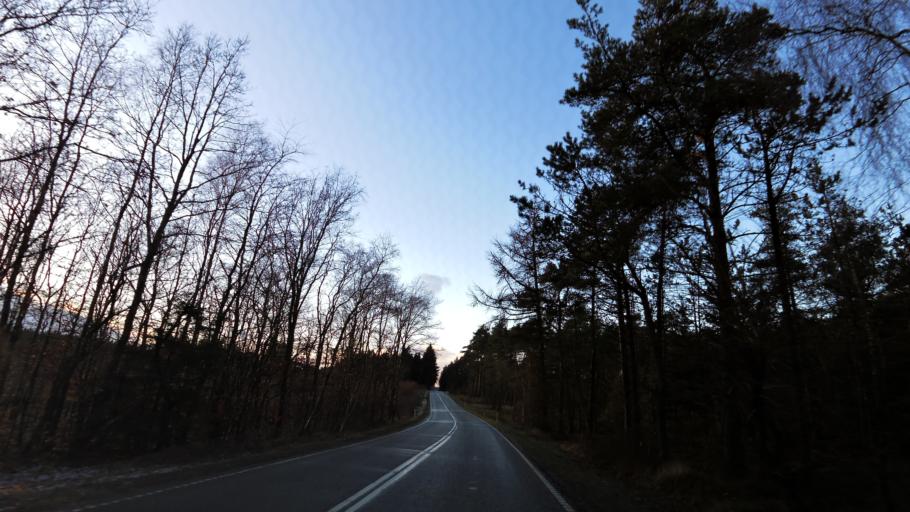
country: DK
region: Central Jutland
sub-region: Ikast-Brande Kommune
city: Brande
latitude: 56.0049
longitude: 9.1614
